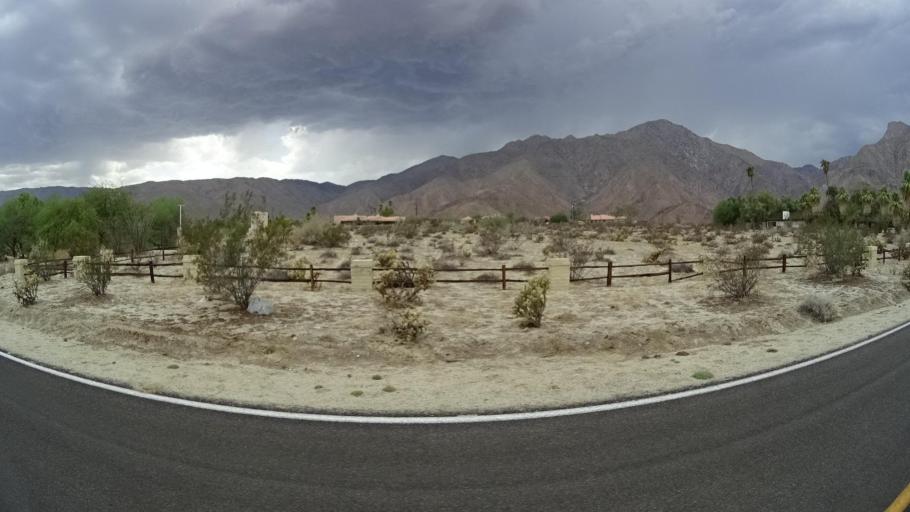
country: US
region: California
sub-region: San Diego County
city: Borrego Springs
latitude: 33.2621
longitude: -116.3961
